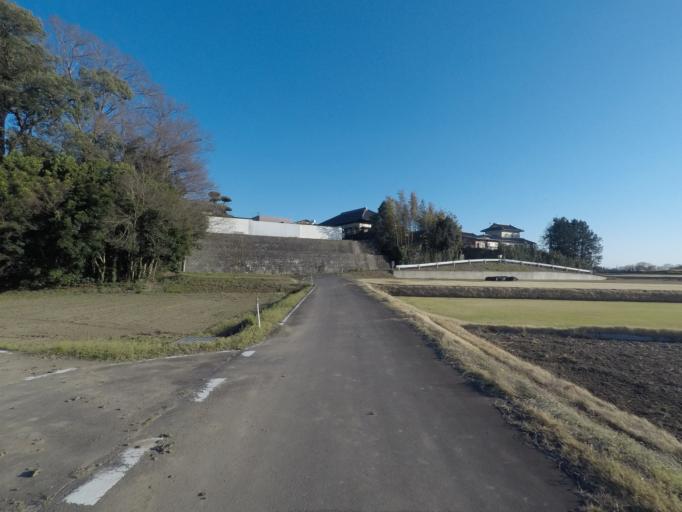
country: JP
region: Ibaraki
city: Ishige
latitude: 36.1570
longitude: 140.0062
